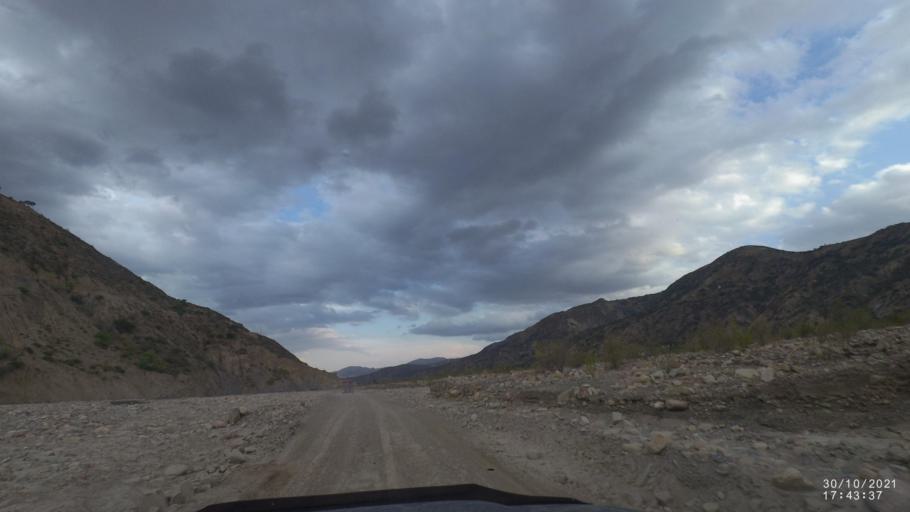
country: BO
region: Cochabamba
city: Sipe Sipe
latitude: -17.5260
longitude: -66.5379
